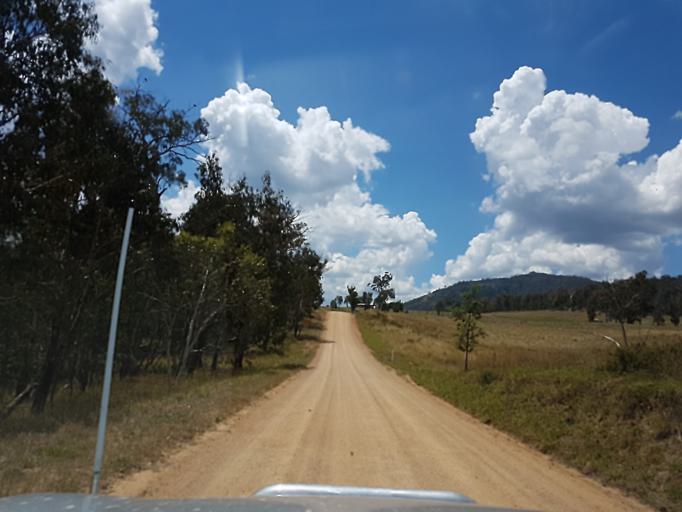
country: AU
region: Victoria
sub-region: Alpine
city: Mount Beauty
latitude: -36.8990
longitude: 147.8728
